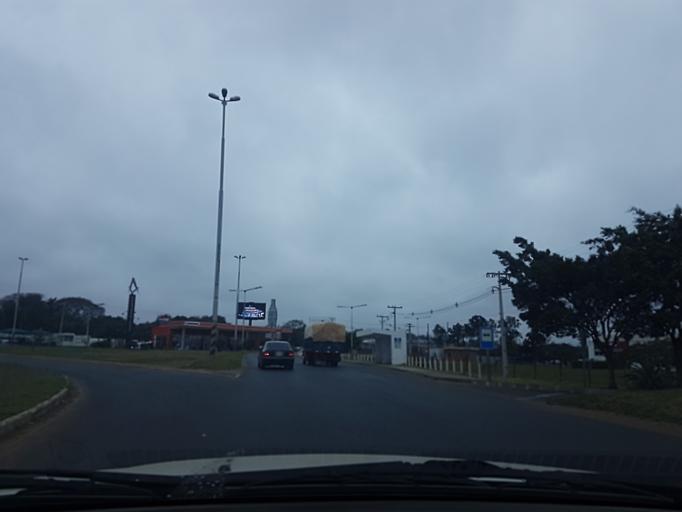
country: PY
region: Central
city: Limpio
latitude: -25.2444
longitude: -57.5123
